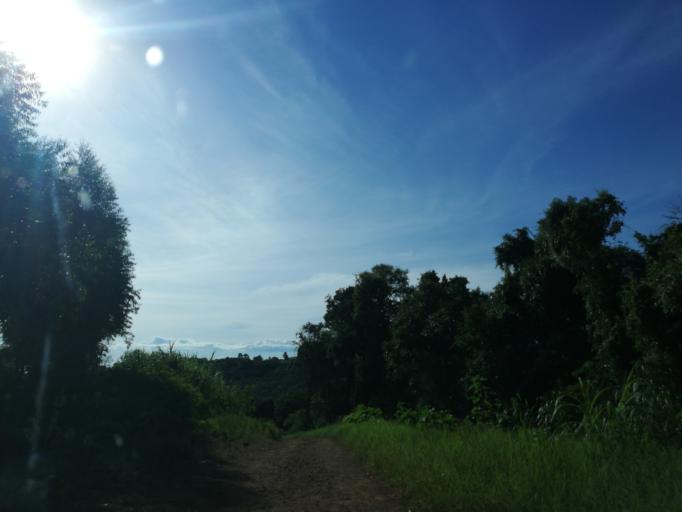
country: AR
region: Misiones
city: Dos de Mayo
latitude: -26.9889
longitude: -54.4958
